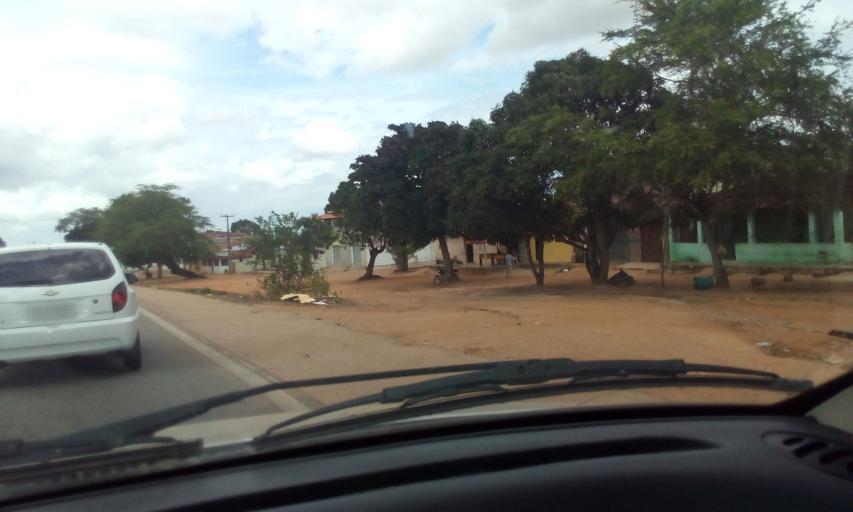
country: BR
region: Rio Grande do Norte
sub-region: Macaiba
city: Macaiba
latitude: -5.9264
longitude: -35.5385
